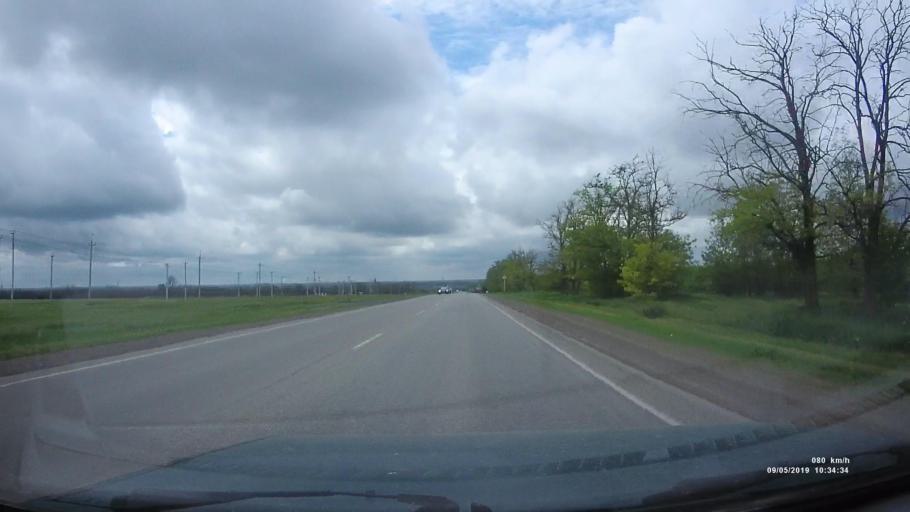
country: RU
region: Rostov
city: Peshkovo
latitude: 47.0528
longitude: 39.4189
